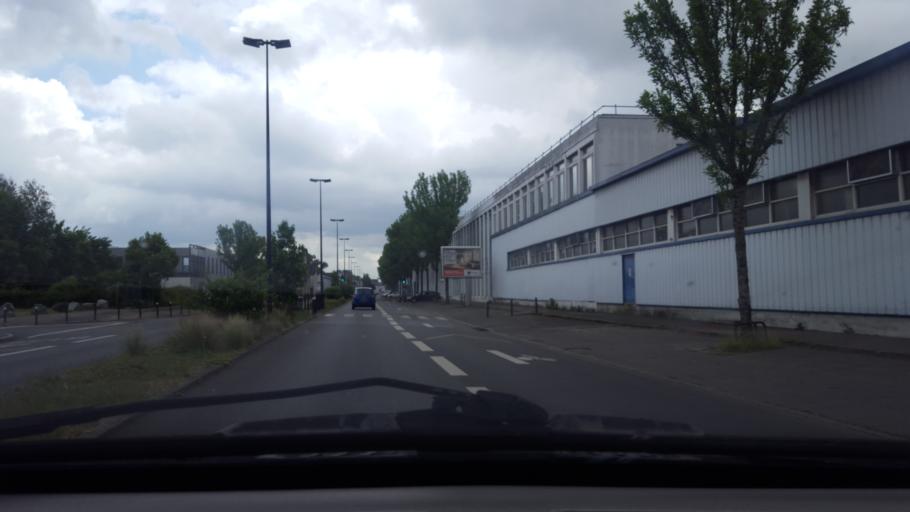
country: FR
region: Pays de la Loire
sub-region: Departement de la Loire-Atlantique
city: Bouguenais
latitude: 47.1982
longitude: -1.6021
